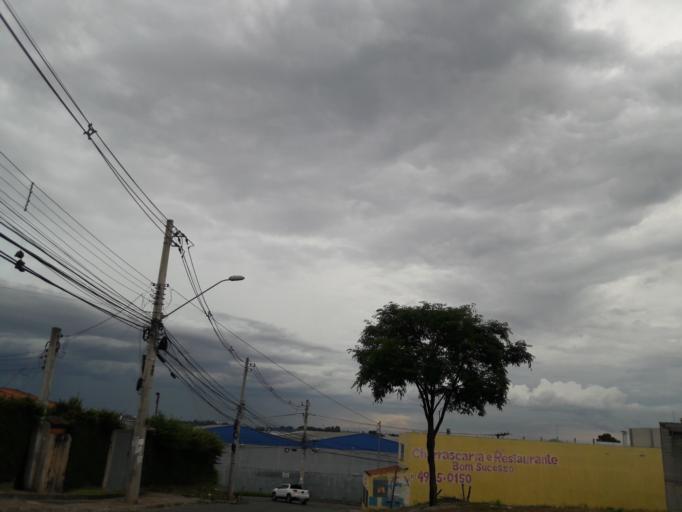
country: BR
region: Sao Paulo
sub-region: Aruja
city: Aruja
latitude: -23.4080
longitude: -46.3994
